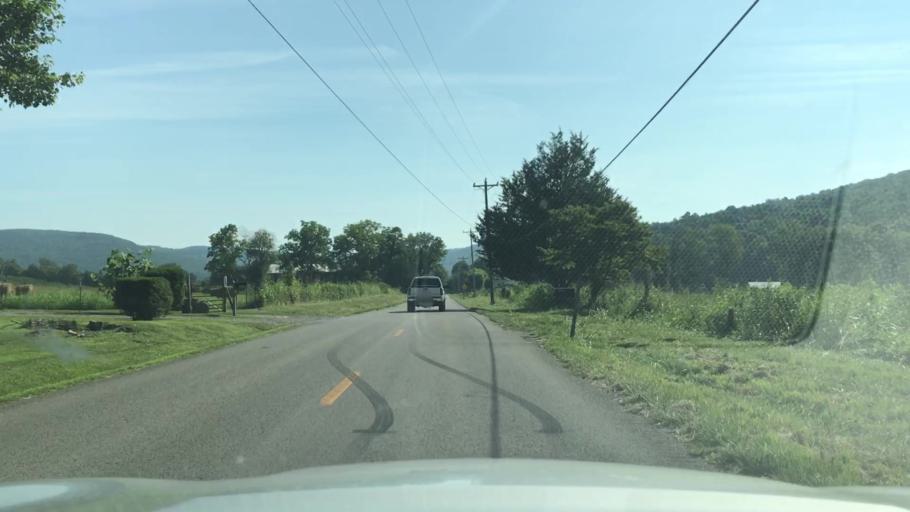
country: US
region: Kentucky
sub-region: Clinton County
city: Albany
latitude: 36.6848
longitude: -85.0597
